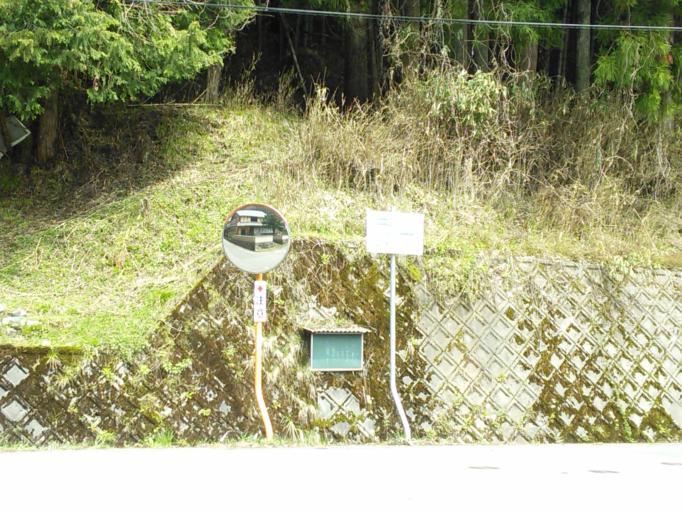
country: JP
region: Kyoto
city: Fukuchiyama
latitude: 35.4213
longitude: 135.0694
